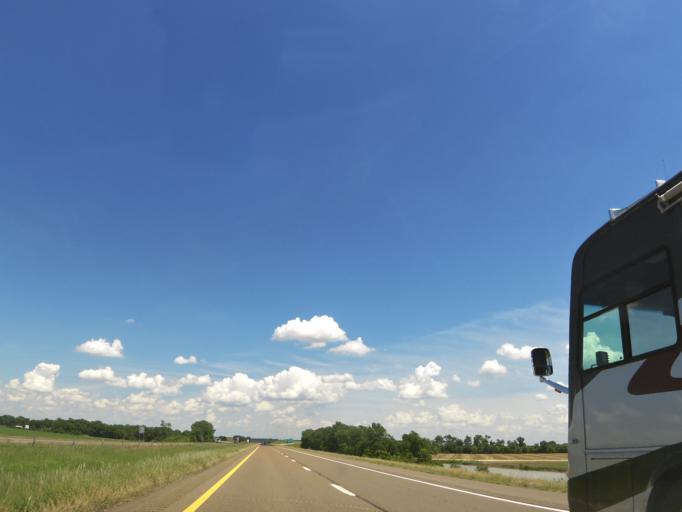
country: US
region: Missouri
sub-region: Pemiscot County
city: Caruthersville
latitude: 36.0954
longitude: -89.5962
